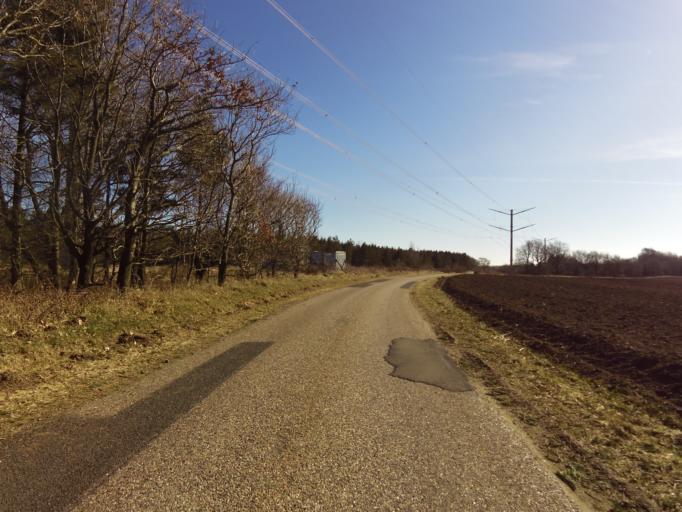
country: DK
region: South Denmark
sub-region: Tonder Kommune
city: Toftlund
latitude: 55.2238
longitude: 9.1465
